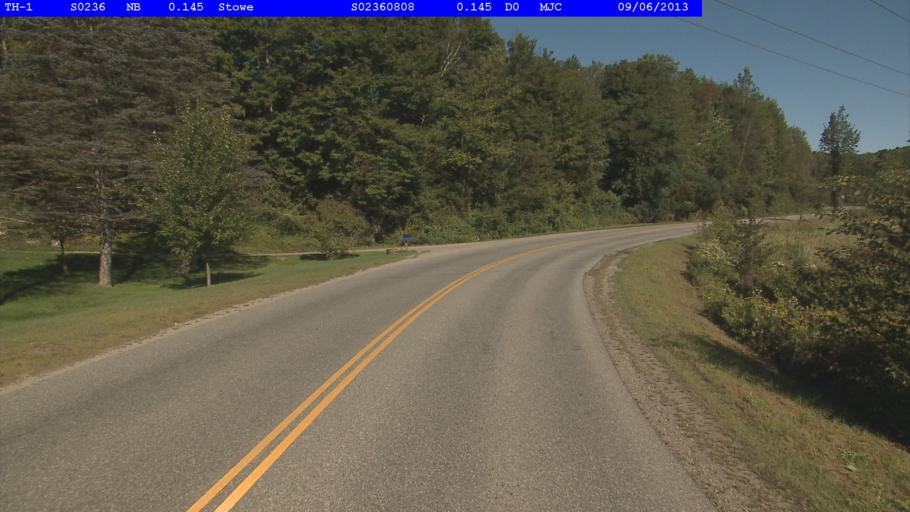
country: US
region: Vermont
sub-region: Washington County
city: Waterbury
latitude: 44.4371
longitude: -72.7138
